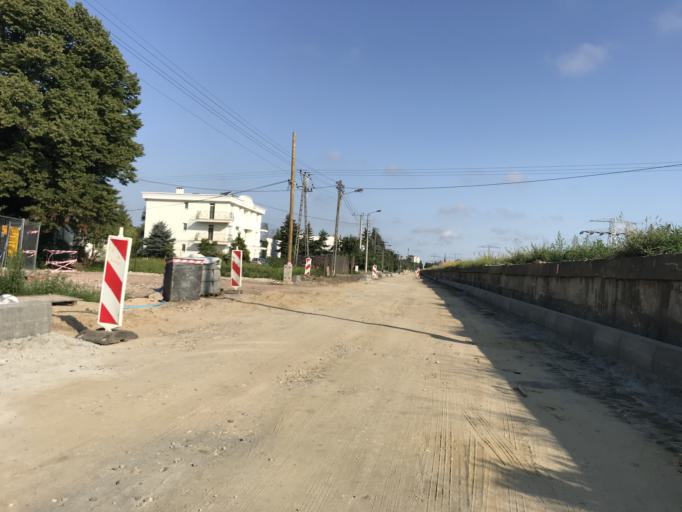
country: PL
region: Pomeranian Voivodeship
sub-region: Gdansk
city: Gdansk
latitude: 54.3415
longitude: 18.6847
